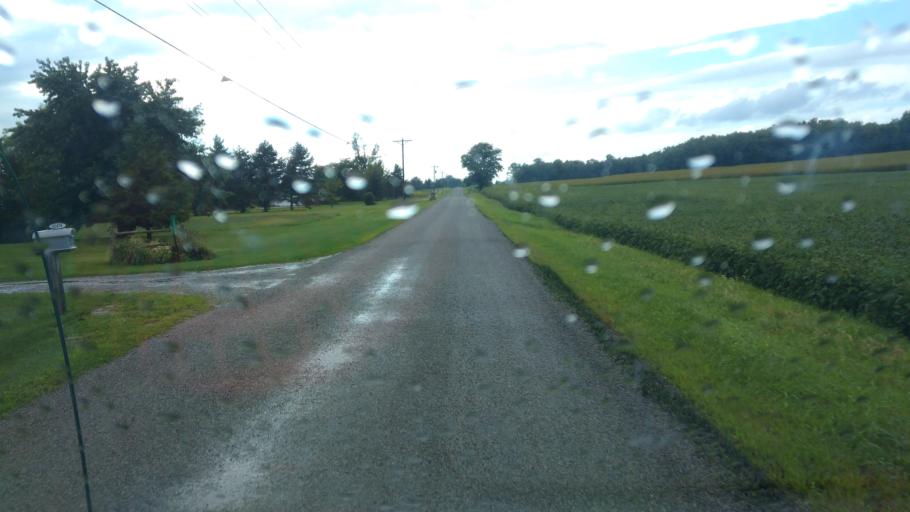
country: US
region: Ohio
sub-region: Hardin County
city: Kenton
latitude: 40.7041
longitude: -83.6445
